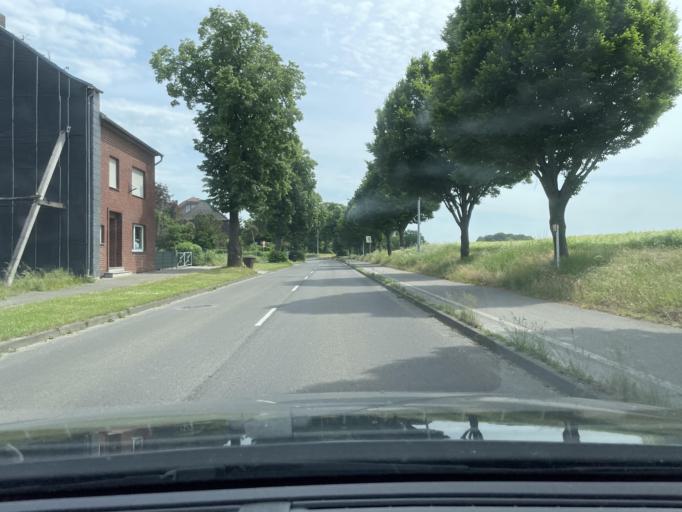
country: DE
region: North Rhine-Westphalia
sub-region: Regierungsbezirk Dusseldorf
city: Schwalmtal
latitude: 51.2042
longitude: 6.3194
